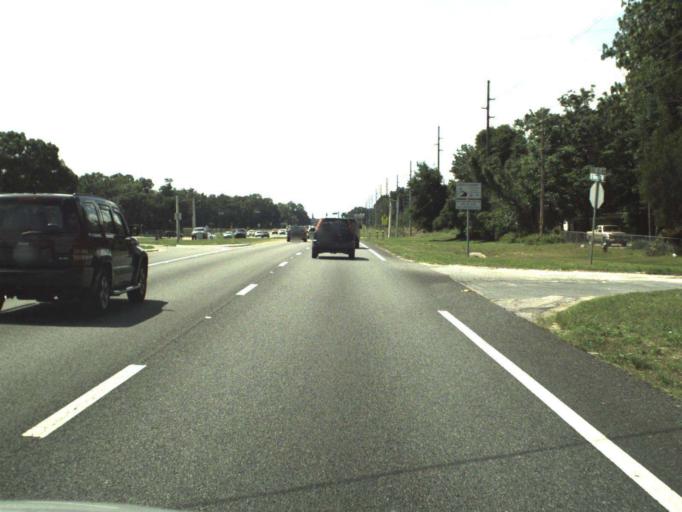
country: US
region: Florida
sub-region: Marion County
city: Silver Springs Shores
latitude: 29.1440
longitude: -82.0640
